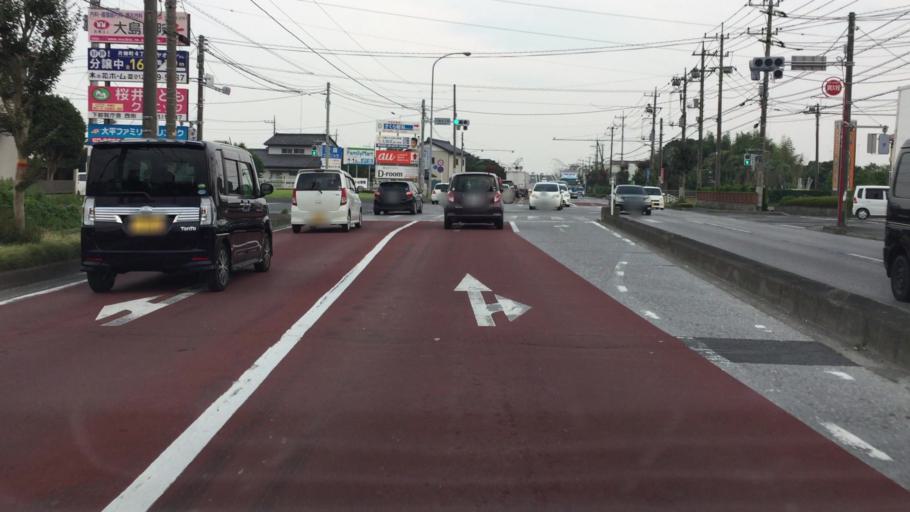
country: JP
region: Tochigi
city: Tochigi
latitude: 36.3687
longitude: 139.7158
